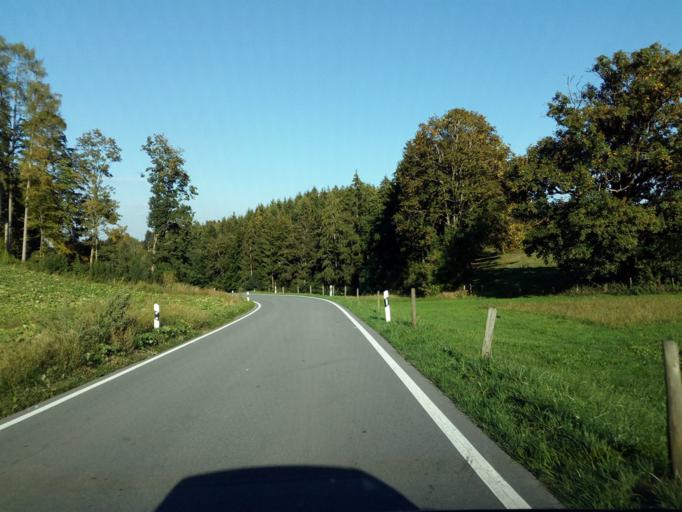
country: CH
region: Bern
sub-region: Seeland District
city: Schupfen
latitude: 47.0259
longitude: 7.3730
